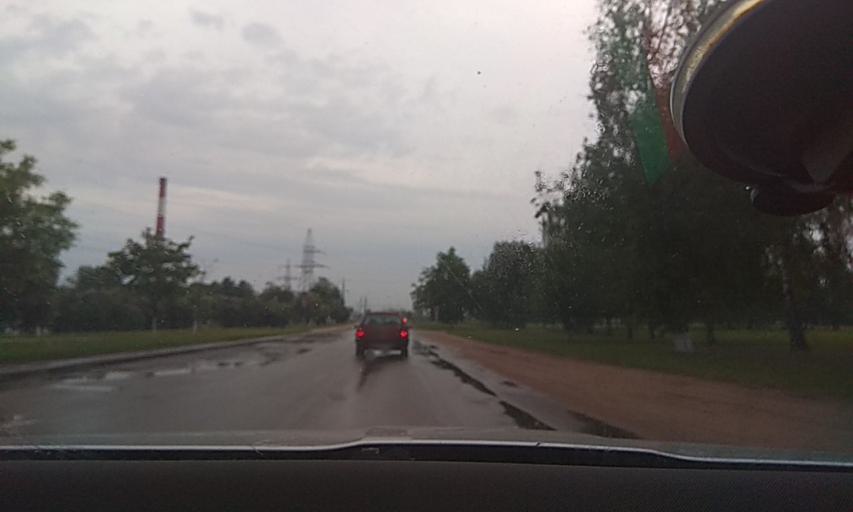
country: BY
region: Grodnenskaya
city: Hrodna
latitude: 53.6750
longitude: 23.8895
